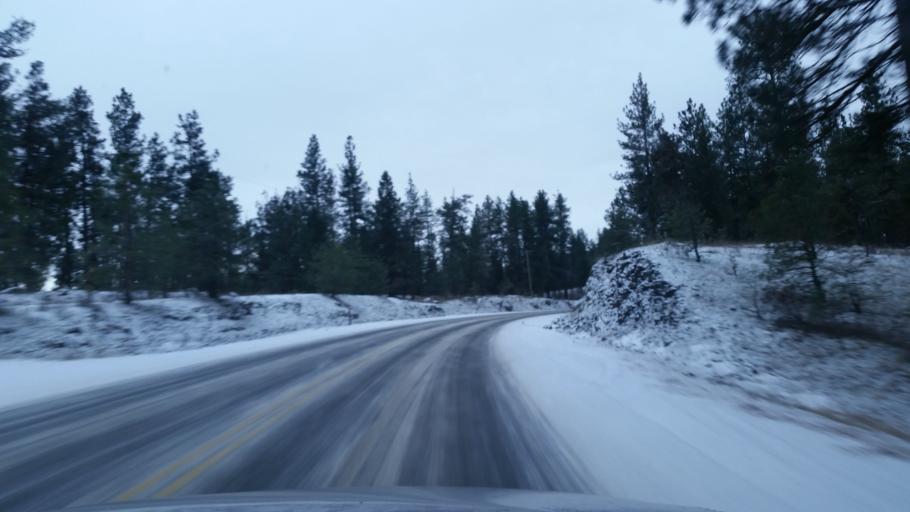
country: US
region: Washington
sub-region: Spokane County
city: Cheney
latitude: 47.4515
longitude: -117.5218
